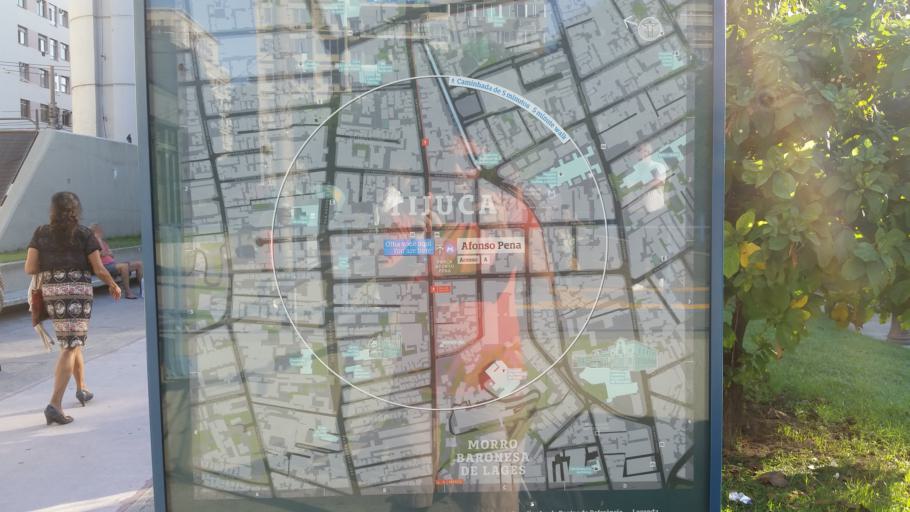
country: BR
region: Rio de Janeiro
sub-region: Rio De Janeiro
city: Rio de Janeiro
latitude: -22.9183
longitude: -43.2180
